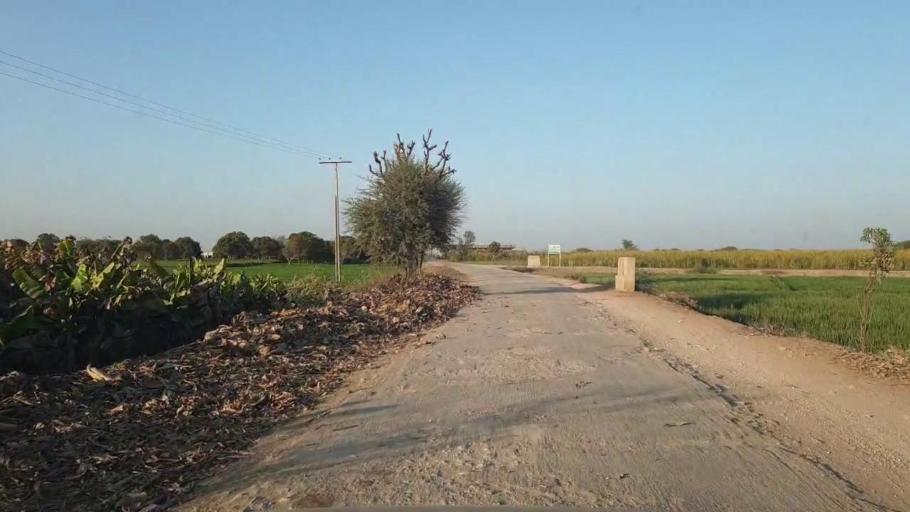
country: PK
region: Sindh
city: Tando Allahyar
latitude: 25.3717
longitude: 68.7477
